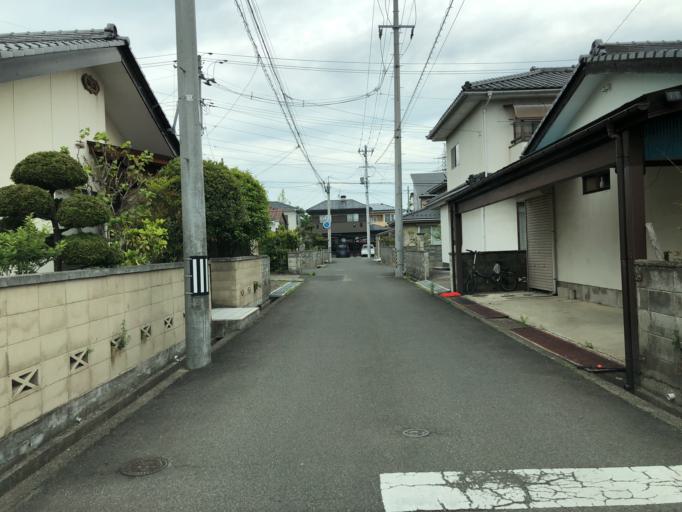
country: JP
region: Fukushima
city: Fukushima-shi
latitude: 37.7976
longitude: 140.4358
